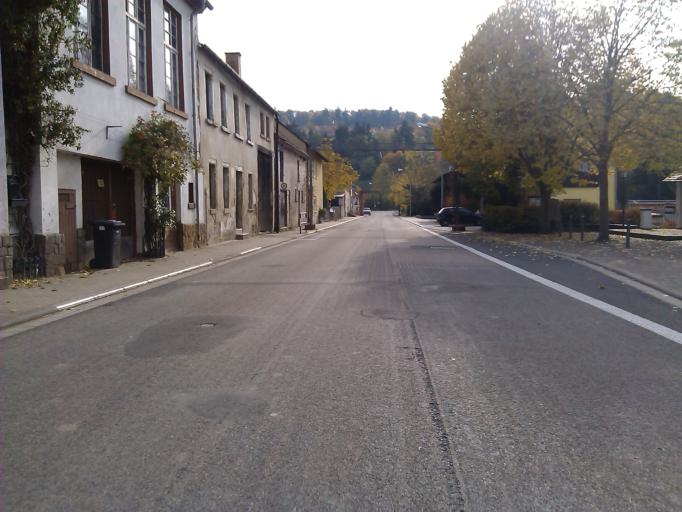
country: DE
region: Rheinland-Pfalz
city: Ginsweiler
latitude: 49.6527
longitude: 7.6477
